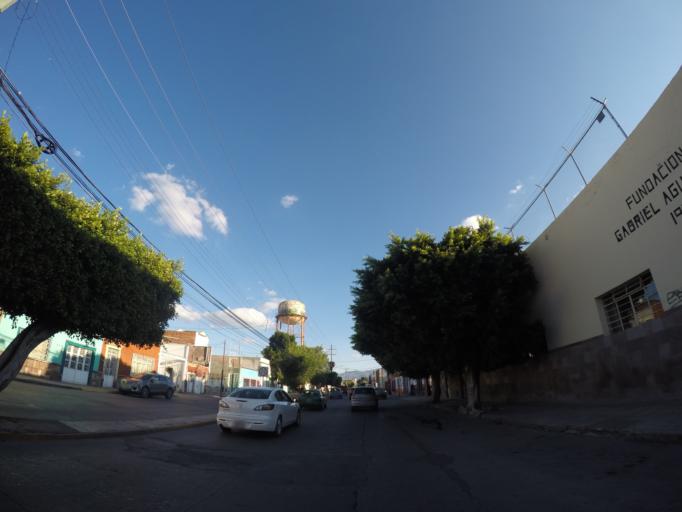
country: MX
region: San Luis Potosi
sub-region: San Luis Potosi
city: San Luis Potosi
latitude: 22.1639
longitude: -100.9803
